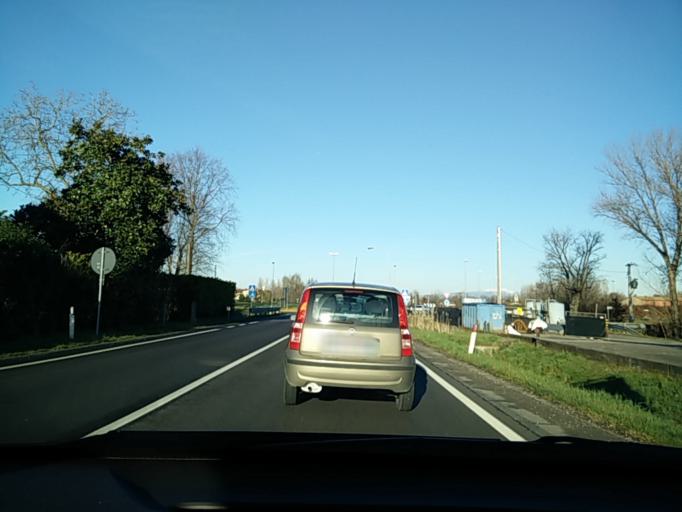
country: IT
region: Veneto
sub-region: Provincia di Treviso
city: Cendon
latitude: 45.6451
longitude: 12.3292
